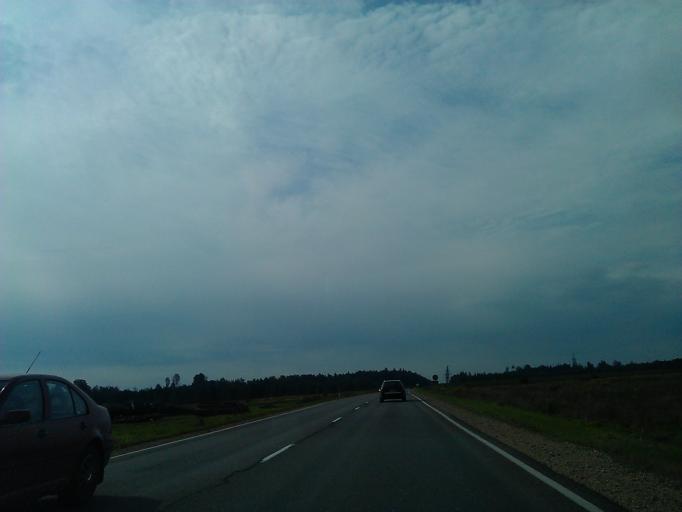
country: LV
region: Salaspils
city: Salaspils
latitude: 56.8846
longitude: 24.4075
